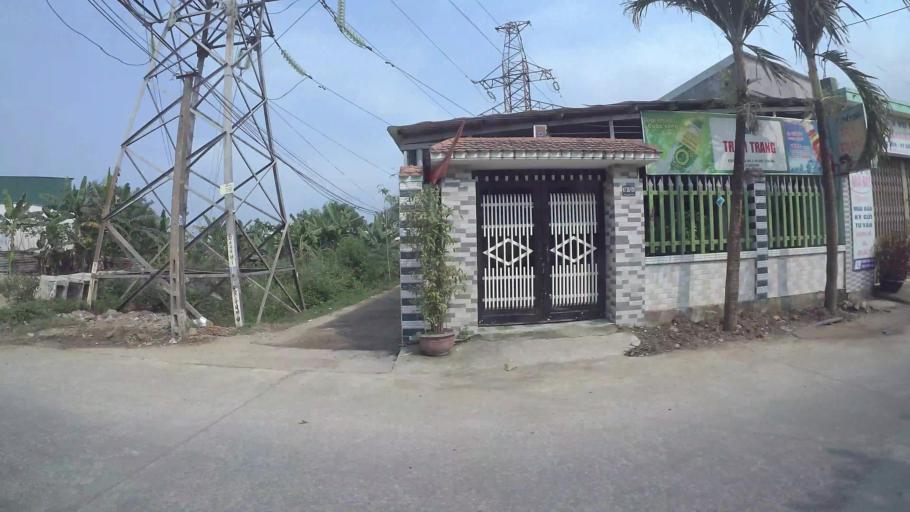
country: VN
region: Da Nang
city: Lien Chieu
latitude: 16.0586
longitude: 108.1569
